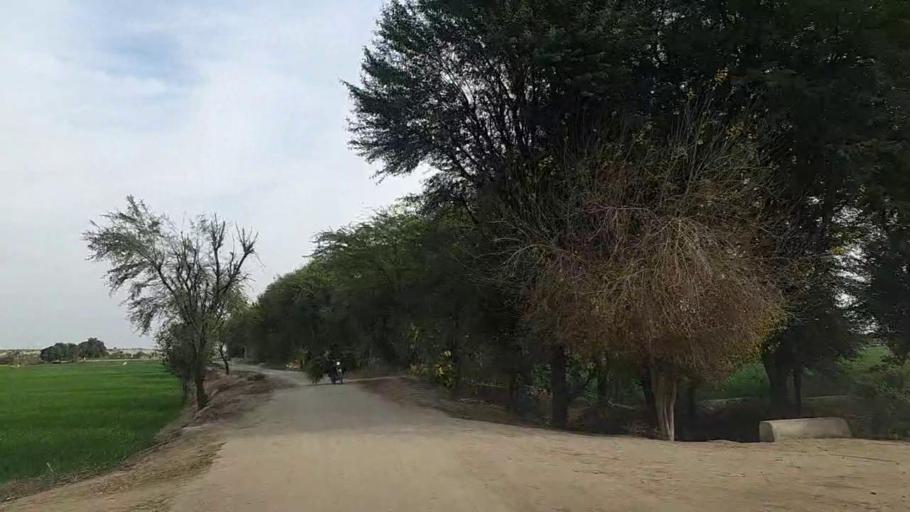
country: PK
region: Sindh
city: Jam Sahib
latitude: 26.4362
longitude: 68.6318
